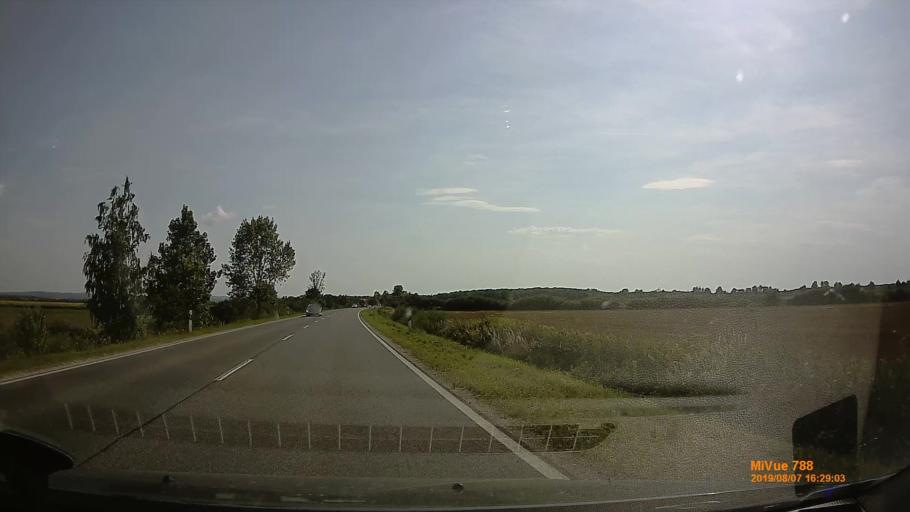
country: HU
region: Zala
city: Lenti
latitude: 46.6864
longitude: 16.5346
